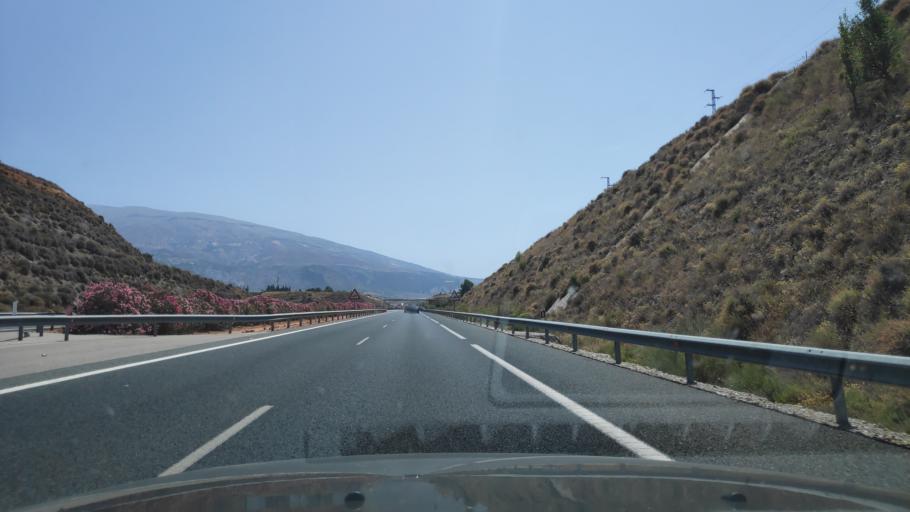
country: ES
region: Andalusia
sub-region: Provincia de Granada
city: Durcal
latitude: 36.9859
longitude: -3.5888
